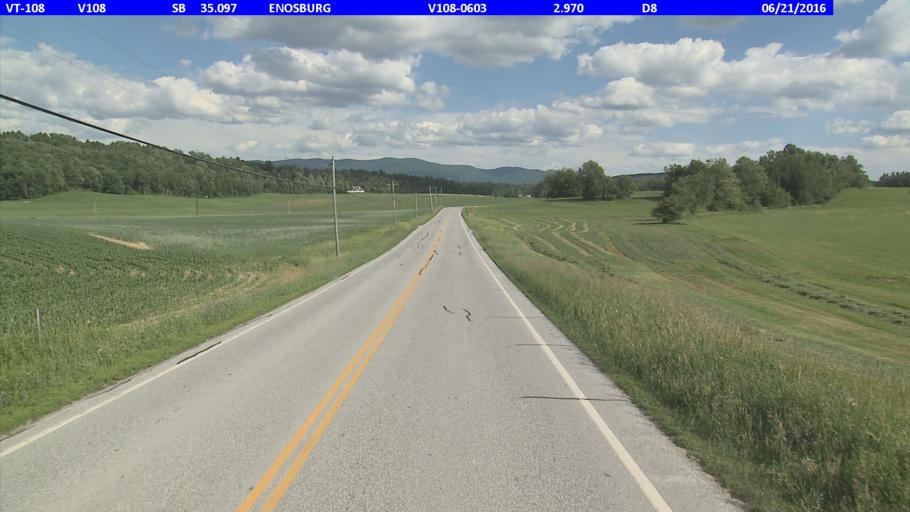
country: US
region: Vermont
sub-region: Franklin County
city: Enosburg Falls
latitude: 44.8796
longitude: -72.7974
